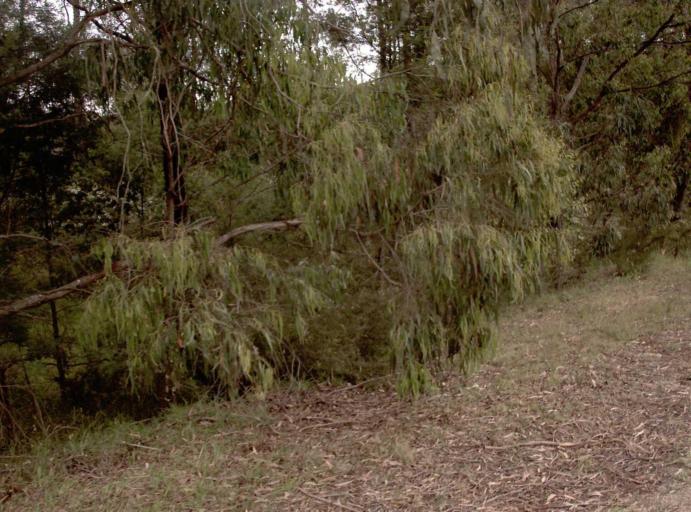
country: AU
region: Victoria
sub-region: East Gippsland
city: Bairnsdale
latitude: -37.7528
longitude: 147.5980
